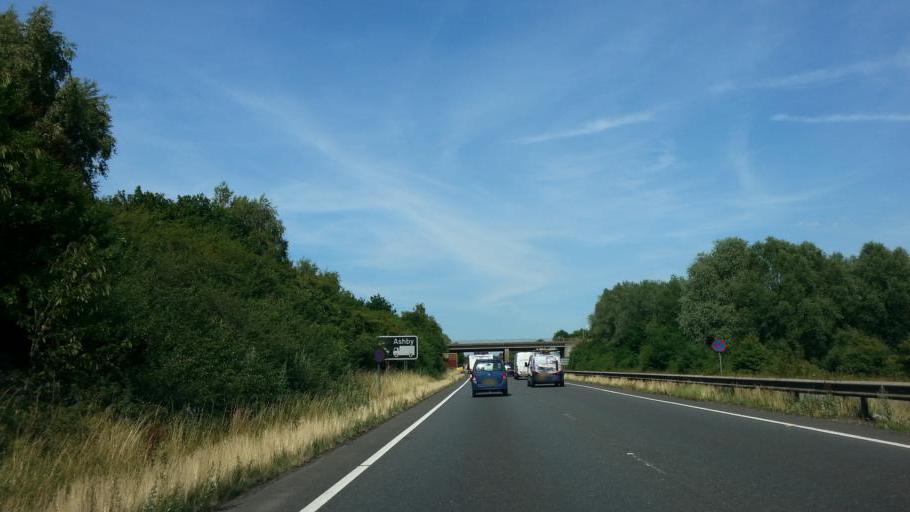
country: GB
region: England
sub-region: Leicestershire
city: Ashby de la Zouch
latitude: 52.7396
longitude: -1.4602
